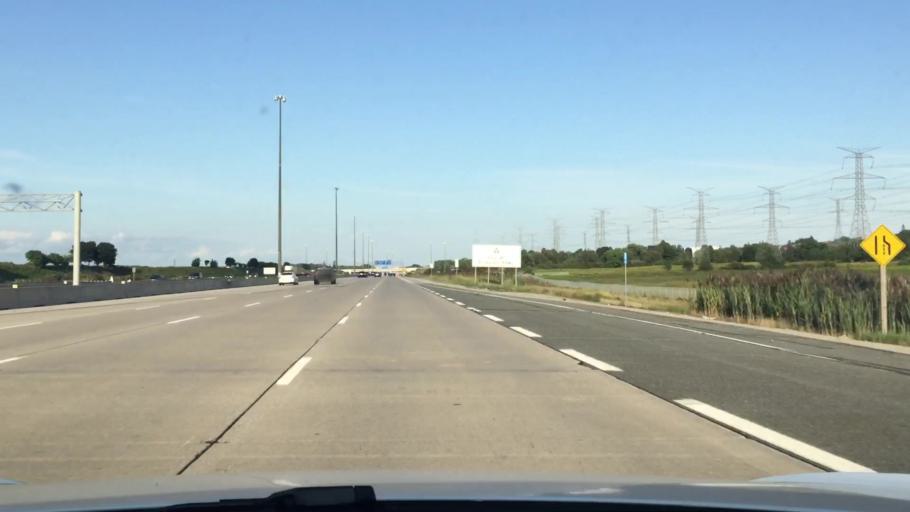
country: CA
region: Ontario
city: Markham
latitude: 43.8525
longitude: -79.2973
